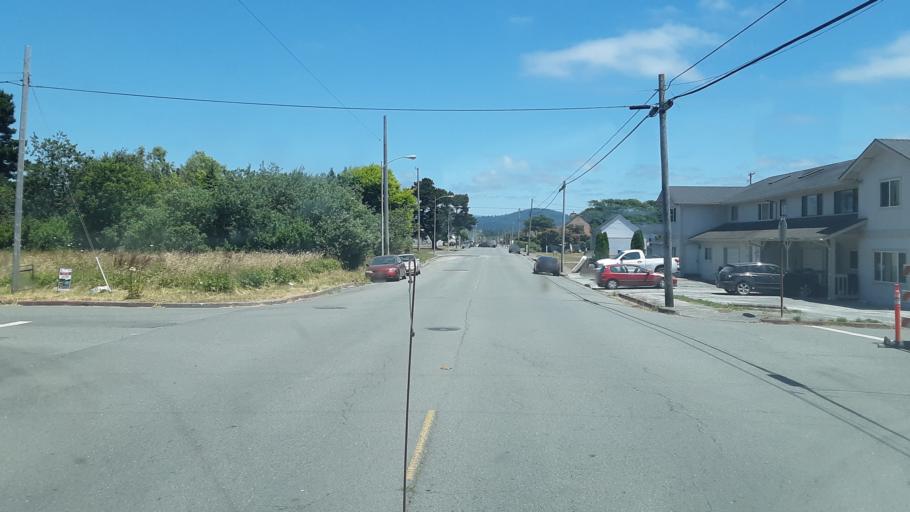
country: US
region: California
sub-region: Del Norte County
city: Crescent City
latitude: 41.7510
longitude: -124.2039
